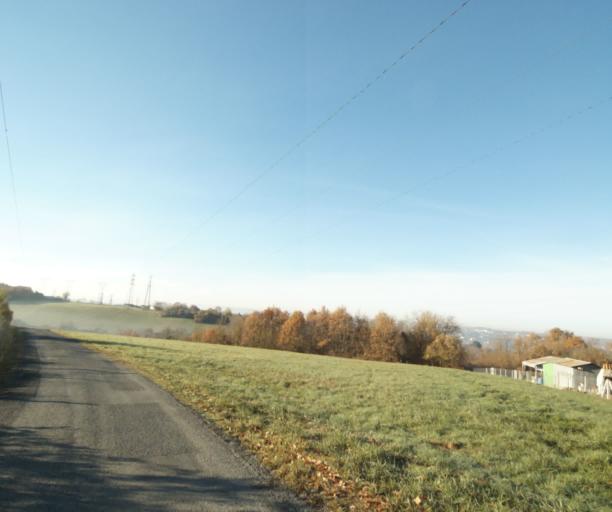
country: FR
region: Poitou-Charentes
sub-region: Departement de la Charente-Maritime
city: Fontcouverte
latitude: 45.7614
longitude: -0.6085
